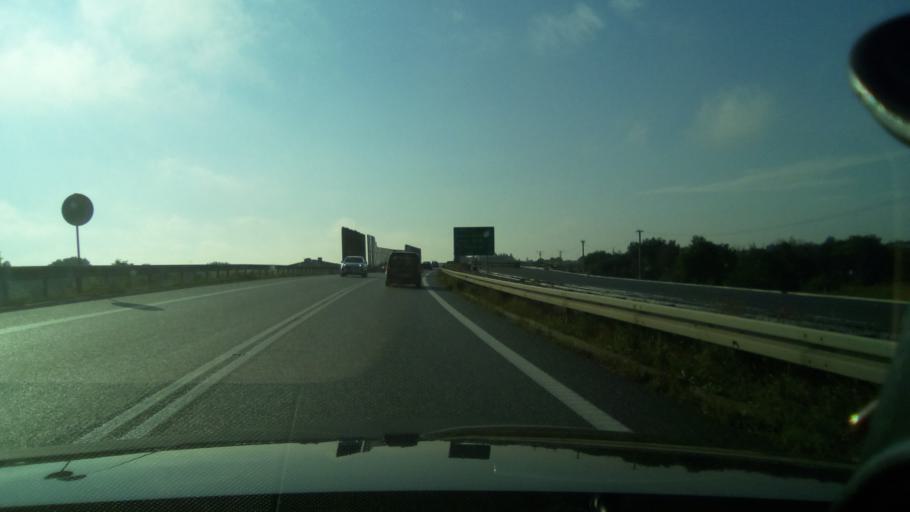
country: PL
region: Silesian Voivodeship
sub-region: Powiat bedzinski
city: Mierzecice
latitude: 50.4479
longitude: 19.1360
